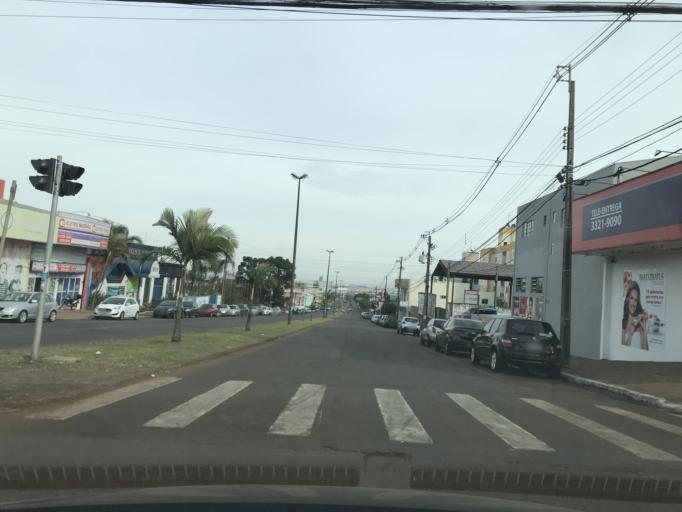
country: BR
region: Parana
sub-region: Cascavel
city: Cascavel
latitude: -24.9542
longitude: -53.4802
